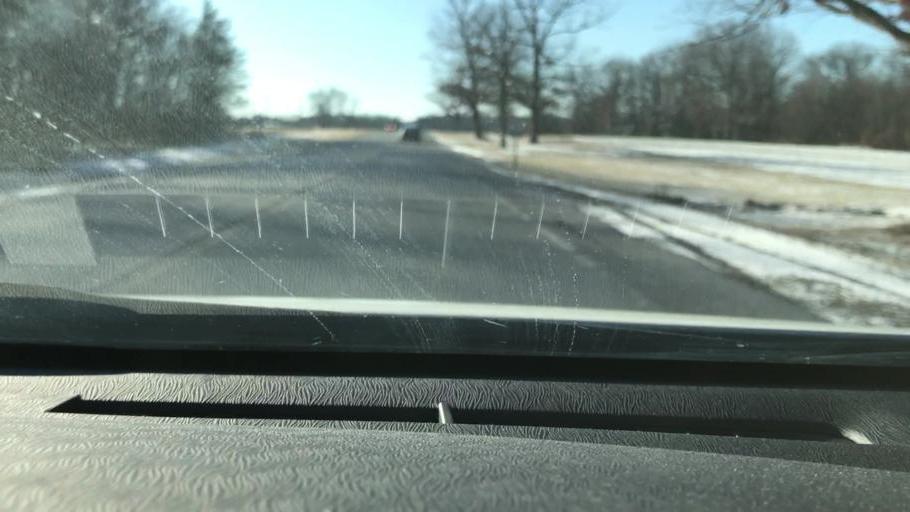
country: US
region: Maryland
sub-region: Prince George's County
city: South Laurel
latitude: 39.0319
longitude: -76.8477
